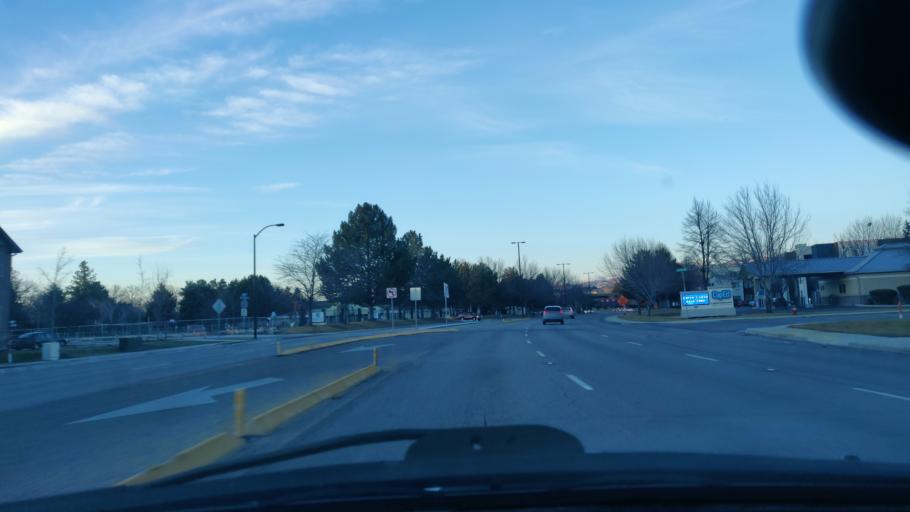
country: US
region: Idaho
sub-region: Ada County
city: Boise
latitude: 43.5929
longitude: -116.1778
